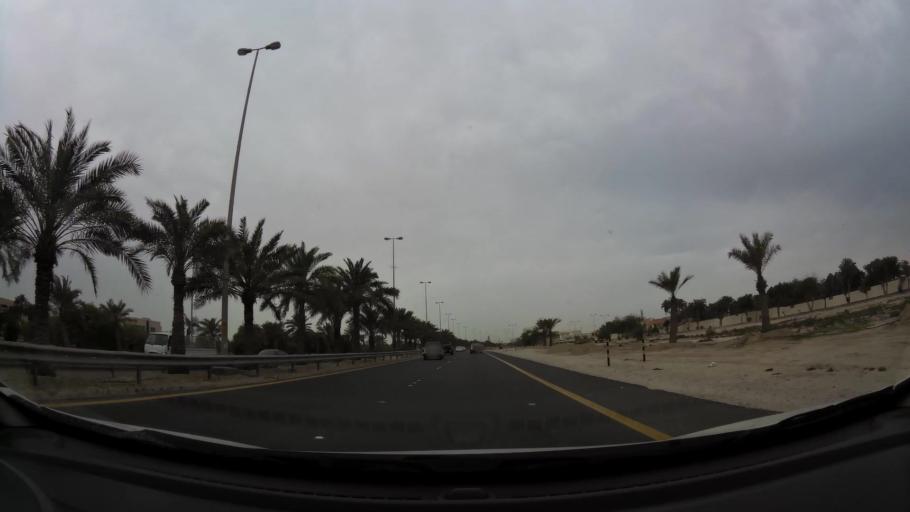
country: BH
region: Northern
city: Ar Rifa'
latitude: 26.1424
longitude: 50.5395
